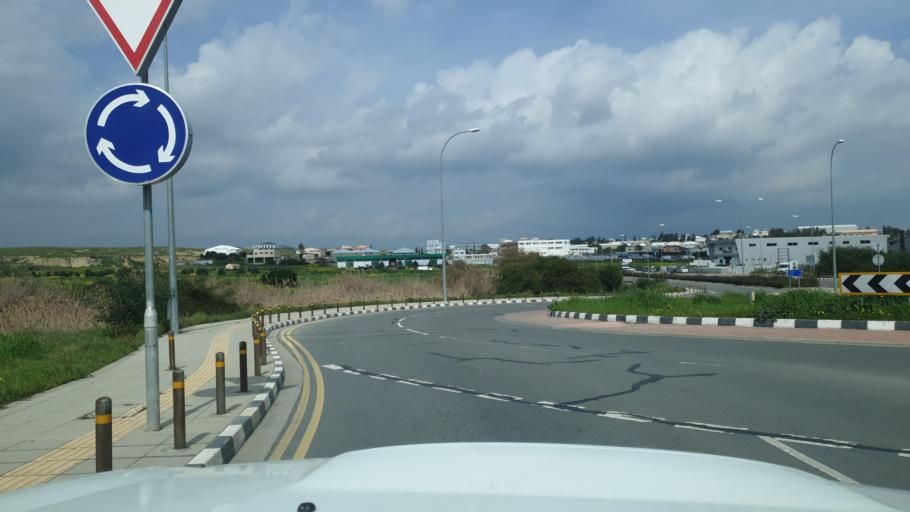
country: CY
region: Lefkosia
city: Tseri
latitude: 35.1153
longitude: 33.3556
